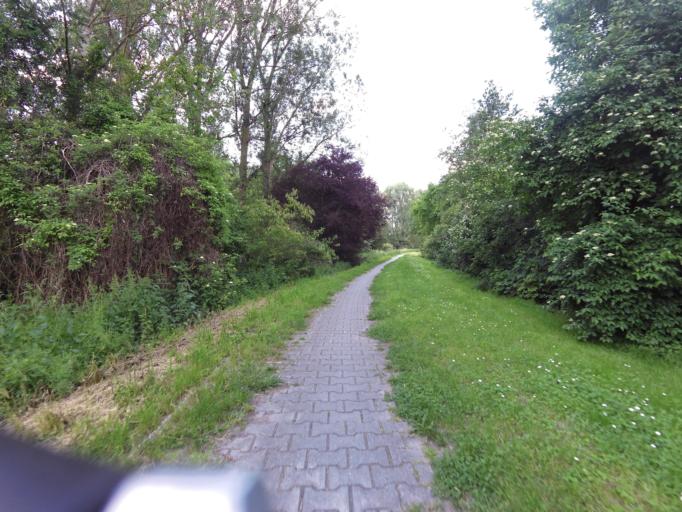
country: DE
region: Hesse
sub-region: Regierungsbezirk Darmstadt
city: Trebur
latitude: 49.9229
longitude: 8.3983
